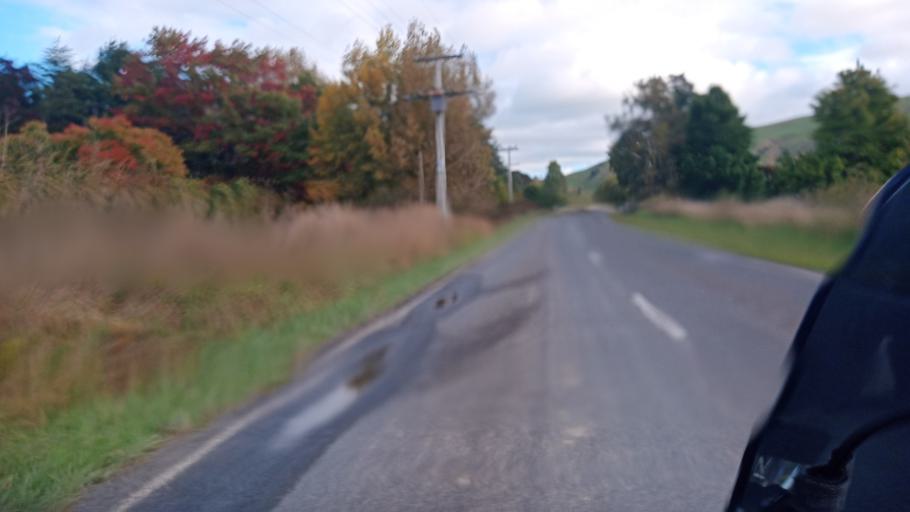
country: NZ
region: Gisborne
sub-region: Gisborne District
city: Gisborne
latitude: -38.5780
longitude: 177.7416
